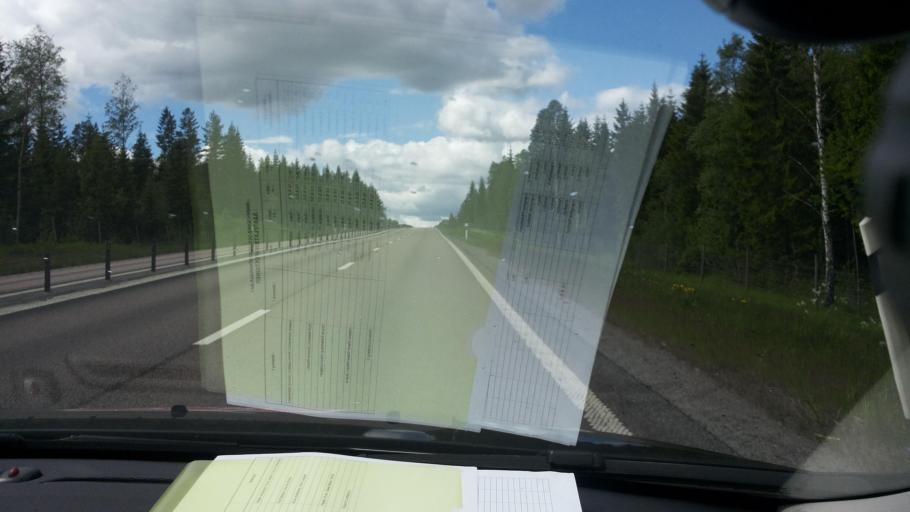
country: SE
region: Vaesternorrland
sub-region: Timra Kommun
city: Soraker
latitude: 62.5346
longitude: 17.5326
